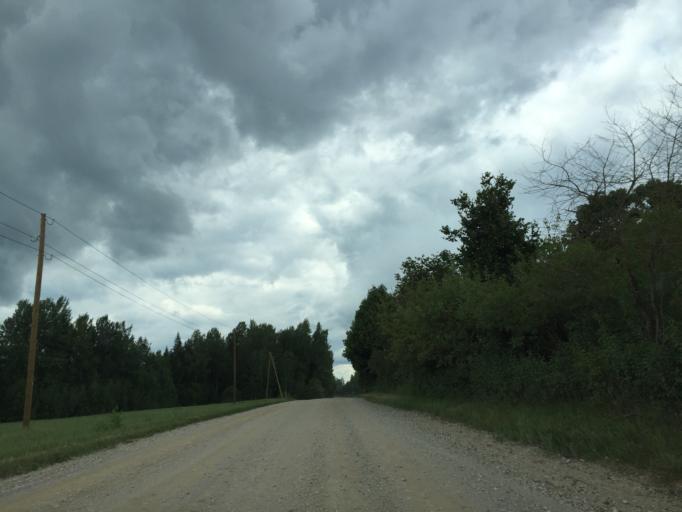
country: LV
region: Malpils
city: Malpils
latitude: 56.8709
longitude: 25.0065
